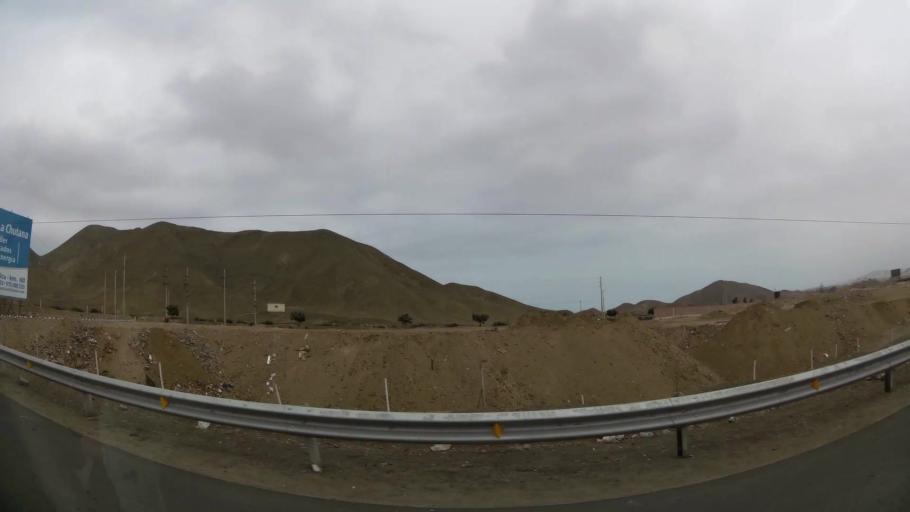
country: PE
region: Lima
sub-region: Lima
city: San Bartolo
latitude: -12.4001
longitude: -76.7567
